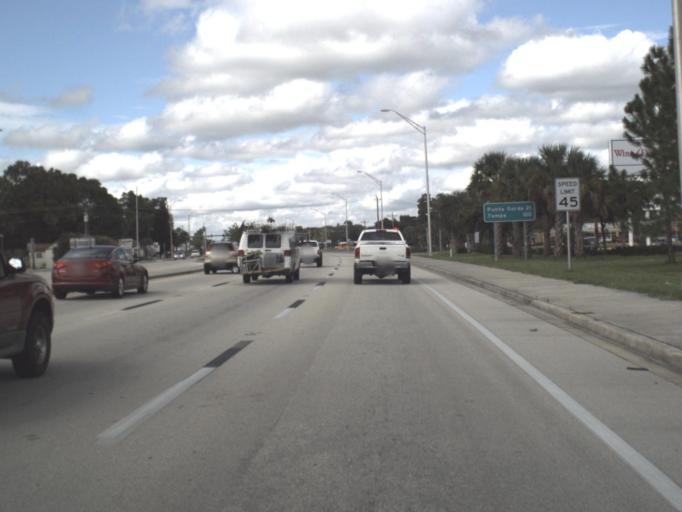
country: US
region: Florida
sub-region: Lee County
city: Palmona Park
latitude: 26.6829
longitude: -81.8836
